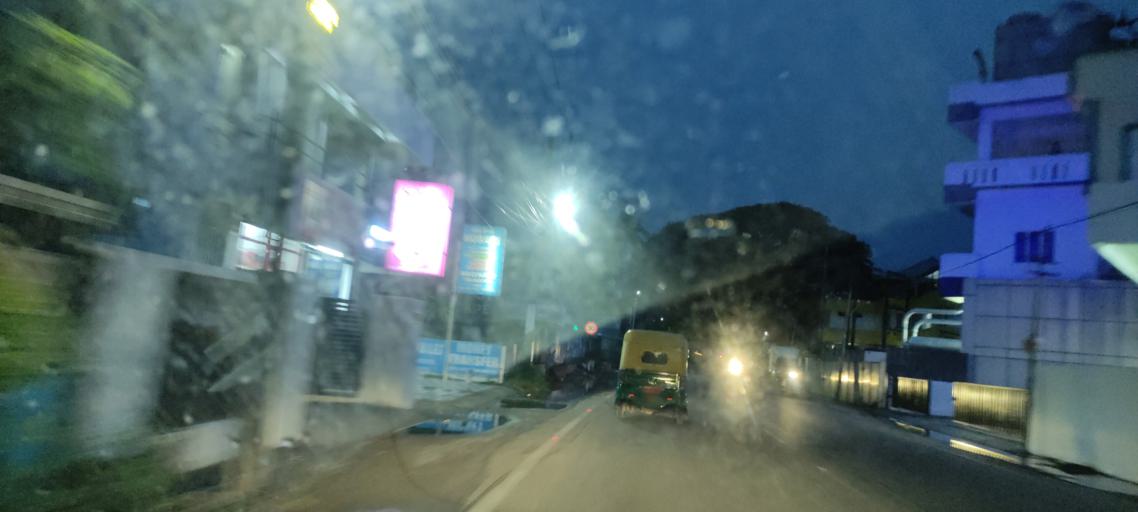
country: IN
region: Kerala
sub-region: Alappuzha
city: Arukutti
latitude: 9.8841
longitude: 76.3015
